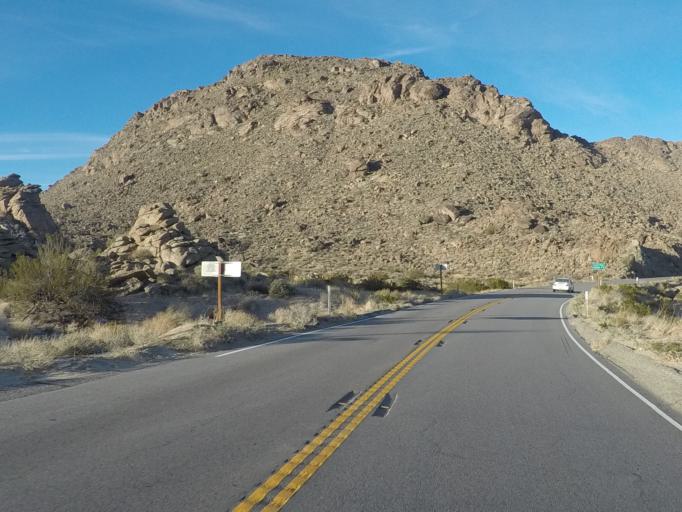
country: US
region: California
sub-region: Riverside County
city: Palm Desert
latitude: 33.6216
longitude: -116.4116
